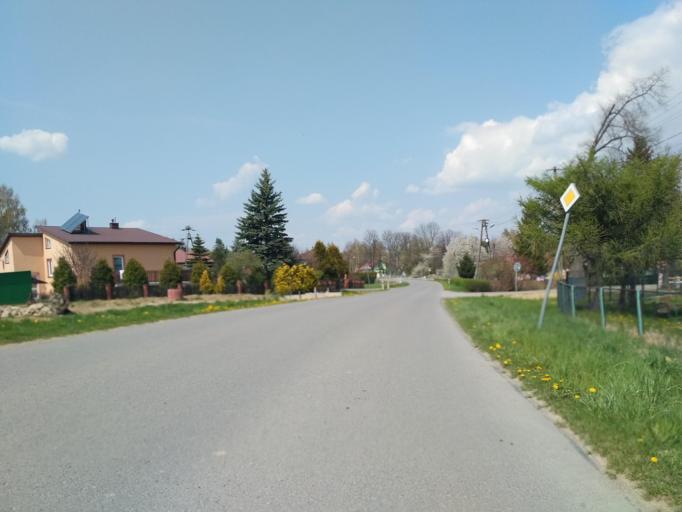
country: PL
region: Subcarpathian Voivodeship
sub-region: Powiat jasielski
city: Tarnowiec
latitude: 49.6680
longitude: 21.5646
